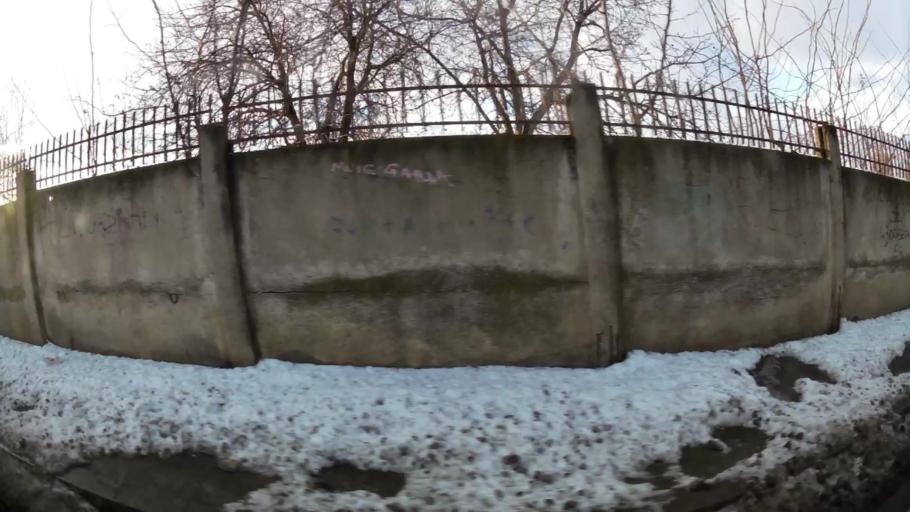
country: RO
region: Ilfov
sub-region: Comuna Popesti-Leordeni
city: Popesti-Leordeni
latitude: 44.3752
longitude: 26.1315
